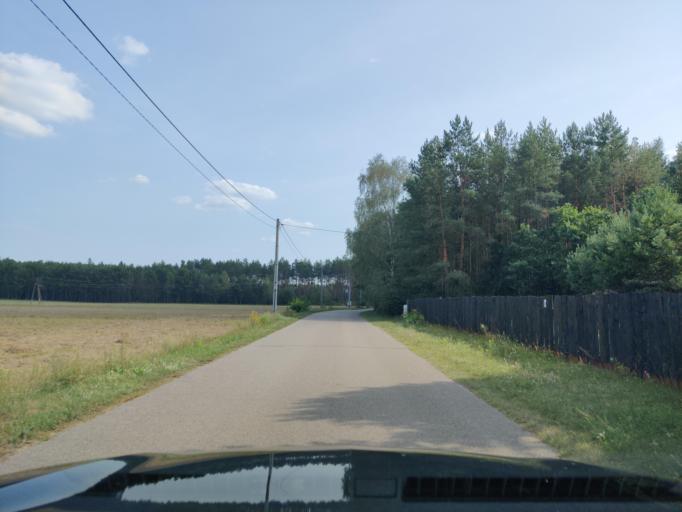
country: PL
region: Masovian Voivodeship
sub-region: Powiat makowski
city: Rozan
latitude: 52.8599
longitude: 21.4489
